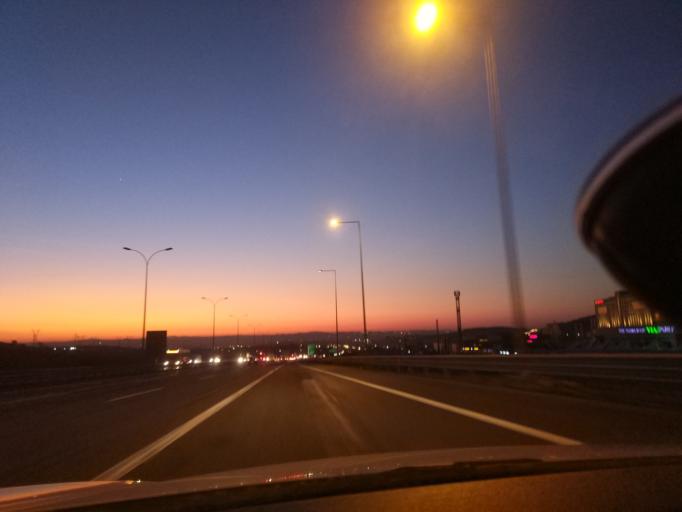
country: TR
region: Istanbul
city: Sultanbeyli
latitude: 40.9419
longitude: 29.3202
